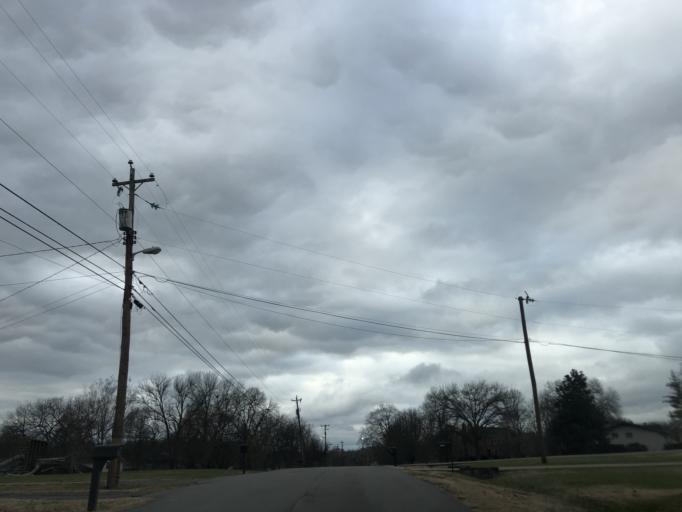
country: US
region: Tennessee
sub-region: Davidson County
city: Goodlettsville
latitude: 36.2946
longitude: -86.6845
